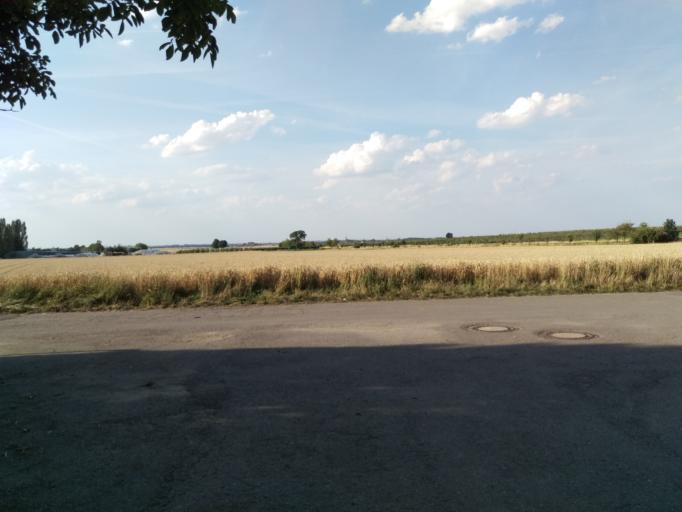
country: DE
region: Lower Saxony
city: Schellerten
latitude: 52.1378
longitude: 10.0652
